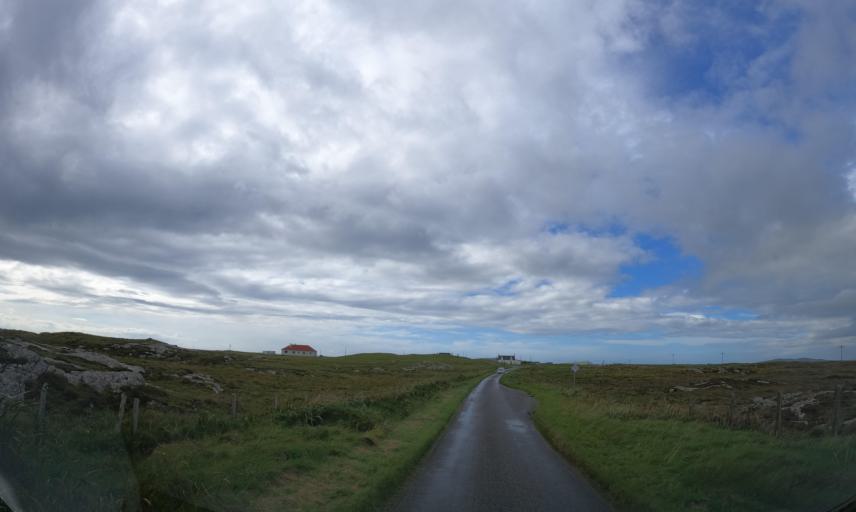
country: GB
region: Scotland
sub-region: Eilean Siar
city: Barra
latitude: 56.4957
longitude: -6.8139
